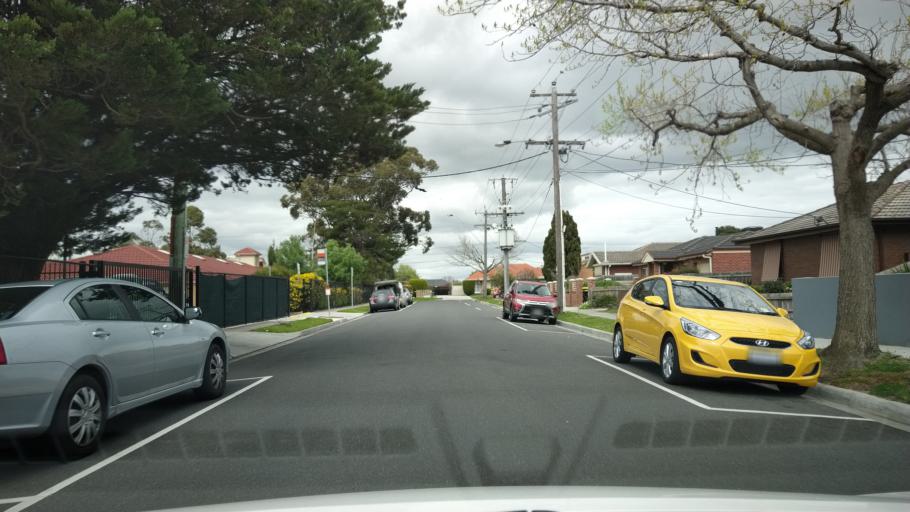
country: AU
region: Victoria
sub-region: Greater Dandenong
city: Noble Park
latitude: -37.9677
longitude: 145.1730
